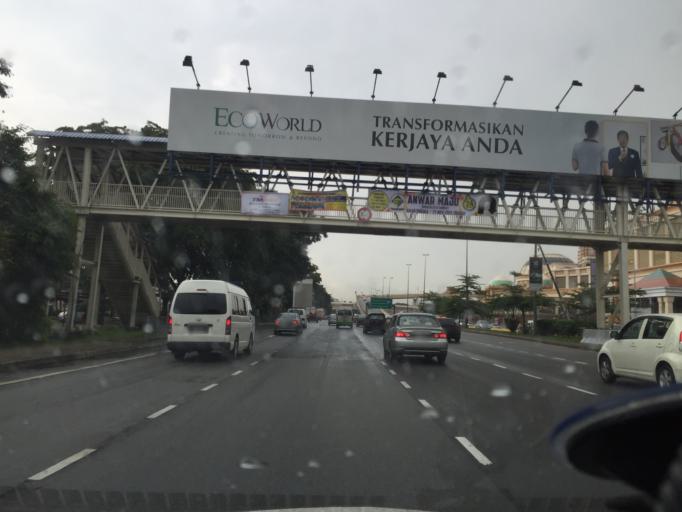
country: MY
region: Selangor
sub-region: Petaling
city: Petaling Jaya
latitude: 3.0736
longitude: 101.6031
